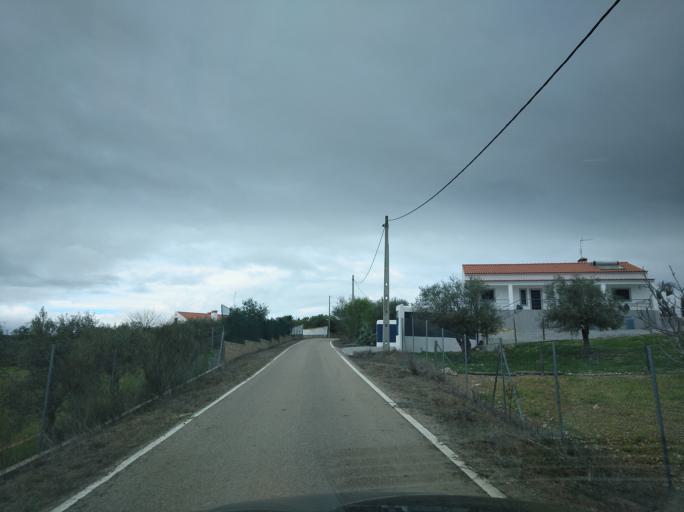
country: PT
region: Portalegre
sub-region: Campo Maior
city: Campo Maior
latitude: 38.9910
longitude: -7.0473
